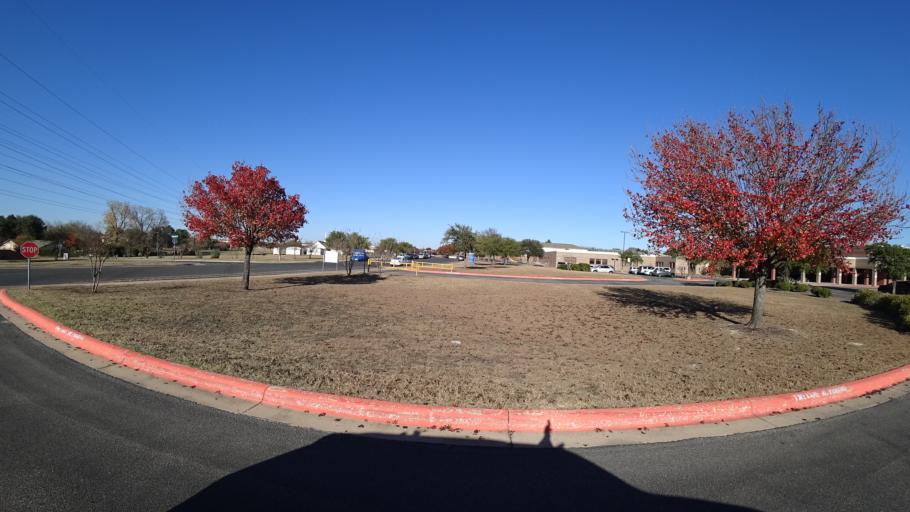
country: US
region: Texas
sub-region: Travis County
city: Wells Branch
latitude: 30.4081
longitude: -97.6882
